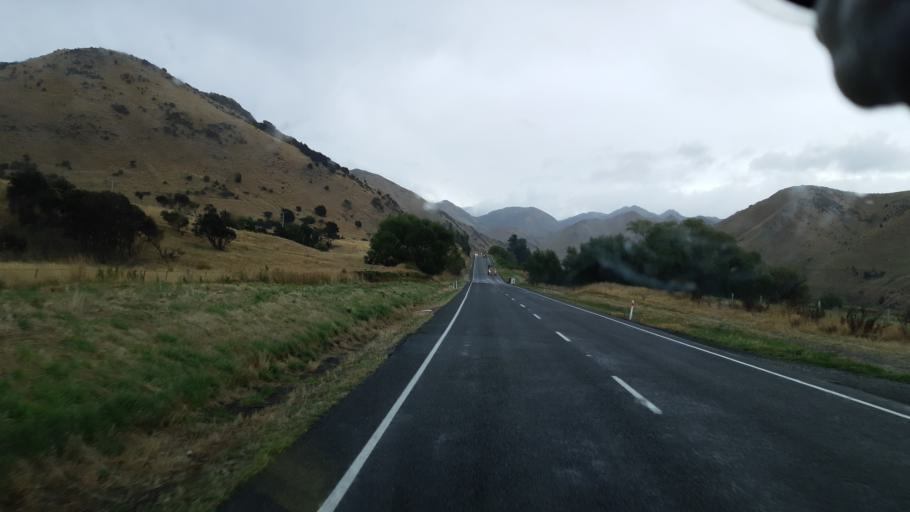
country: NZ
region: Canterbury
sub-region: Hurunui District
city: Amberley
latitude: -42.6733
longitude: 172.7780
